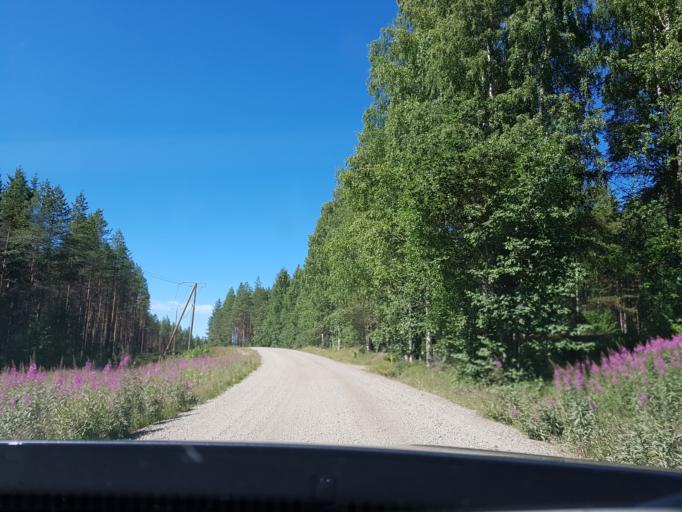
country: FI
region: Kainuu
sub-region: Kehys-Kainuu
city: Kuhmo
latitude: 64.1761
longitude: 29.6286
